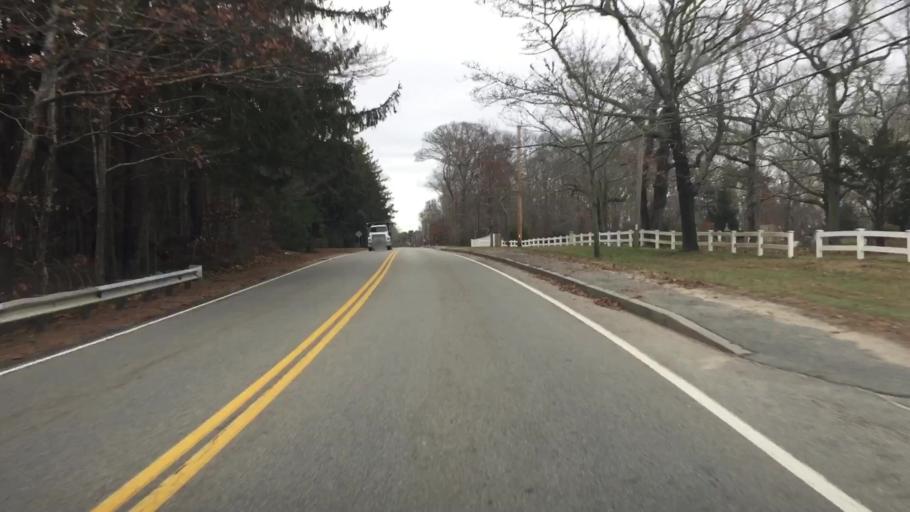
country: US
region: Massachusetts
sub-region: Barnstable County
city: Teaticket
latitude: 41.5682
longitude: -70.6071
